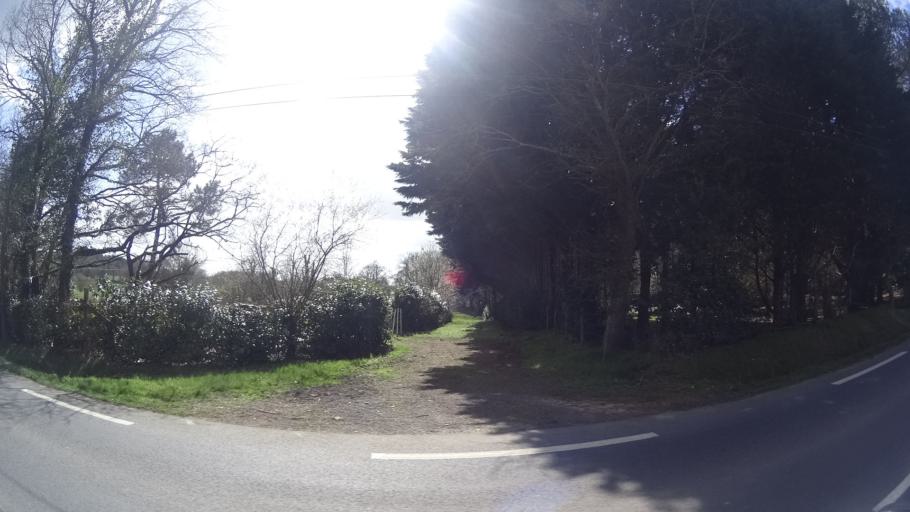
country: FR
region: Brittany
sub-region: Departement du Morbihan
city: Saint-Jacut-les-Pins
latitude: 47.6478
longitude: -2.2110
